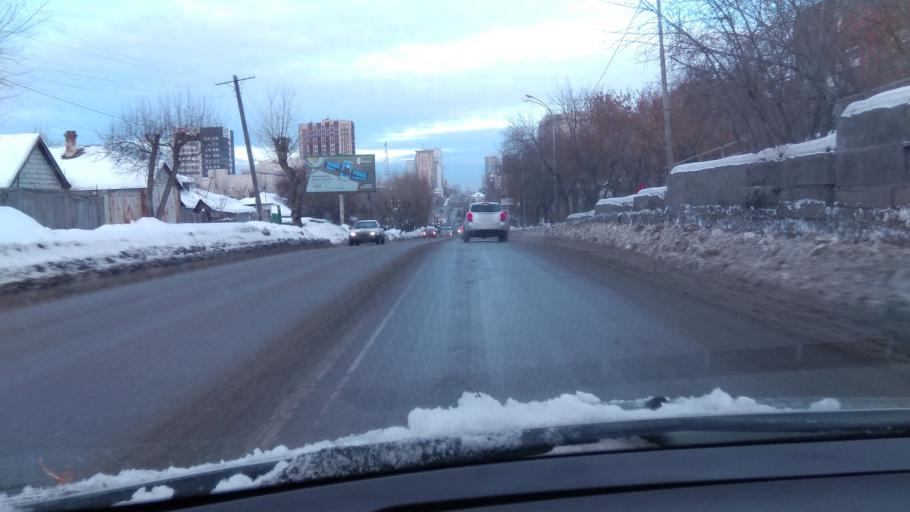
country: RU
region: Sverdlovsk
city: Yekaterinburg
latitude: 56.8094
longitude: 60.5915
